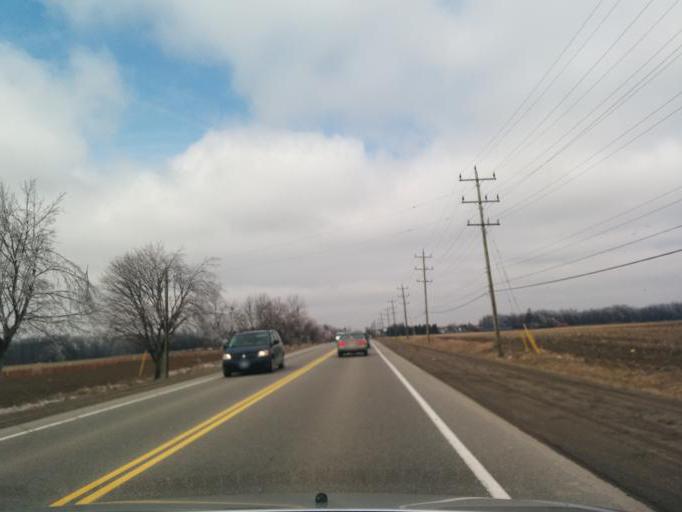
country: CA
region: Ontario
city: Waterloo
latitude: 43.5191
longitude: -80.5569
